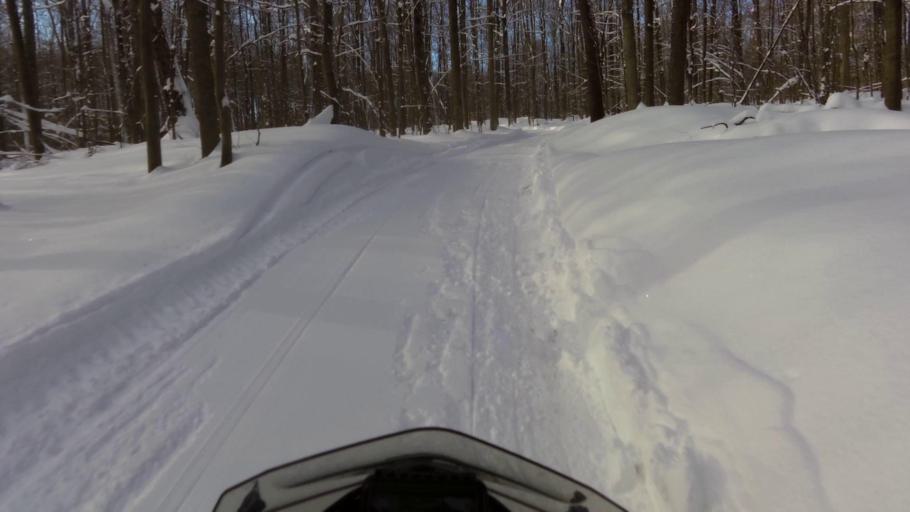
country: US
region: New York
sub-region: Chautauqua County
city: Falconer
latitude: 42.2452
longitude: -79.1514
